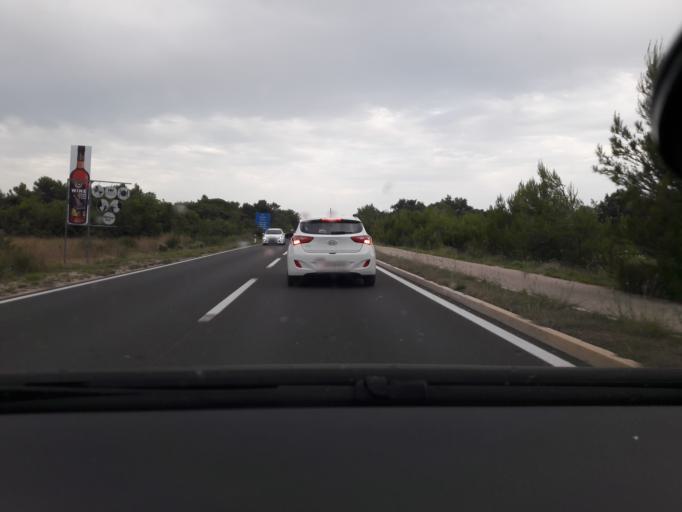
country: HR
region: Zadarska
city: Nin
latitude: 44.1882
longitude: 15.1823
